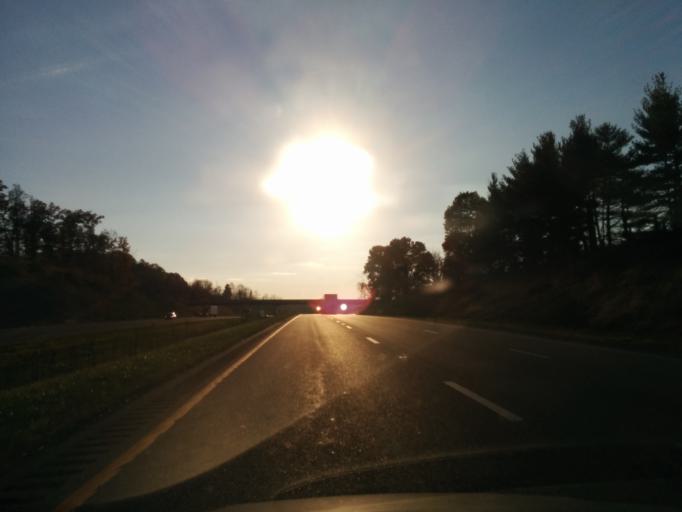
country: US
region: Virginia
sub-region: Rockbridge County
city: East Lexington
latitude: 37.8733
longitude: -79.3135
